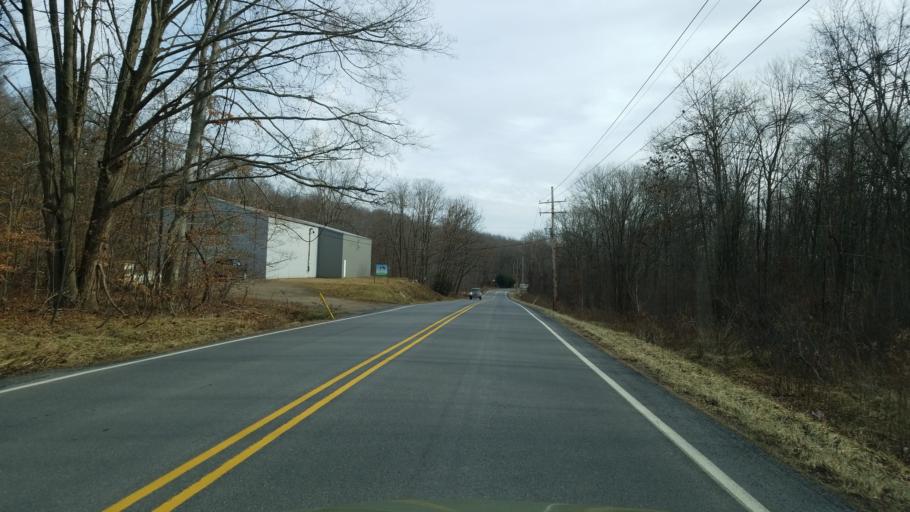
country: US
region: Pennsylvania
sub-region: Indiana County
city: Johnsonburg
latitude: 40.8903
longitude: -78.7857
